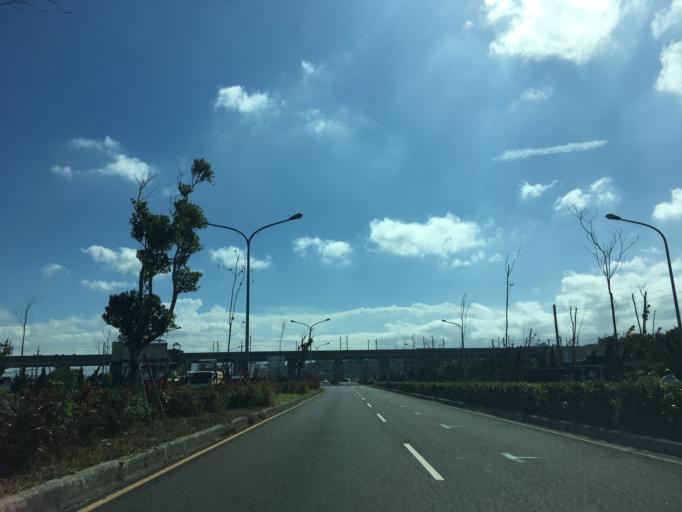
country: TW
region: Taiwan
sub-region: Hsinchu
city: Zhubei
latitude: 24.7871
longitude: 121.0317
